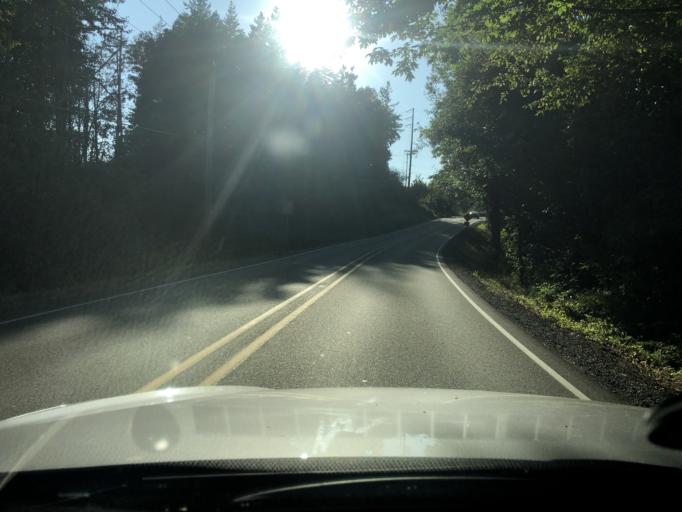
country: US
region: Washington
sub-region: Pierce County
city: Bonney Lake
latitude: 47.2487
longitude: -122.1743
